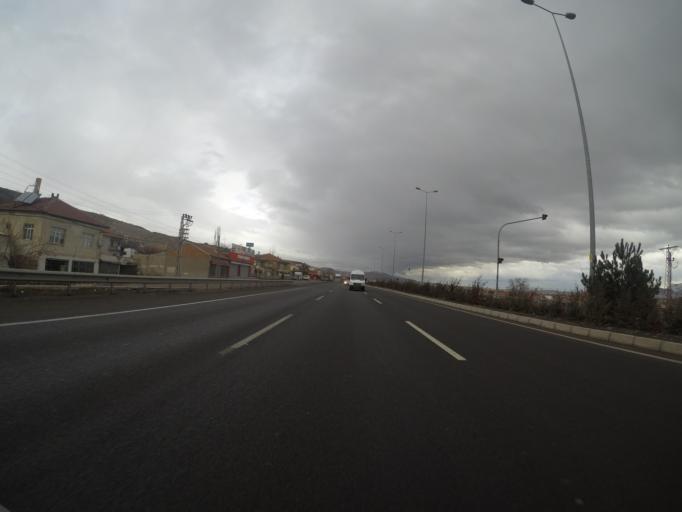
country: TR
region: Kayseri
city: Incesu
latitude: 38.7364
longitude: 35.2900
